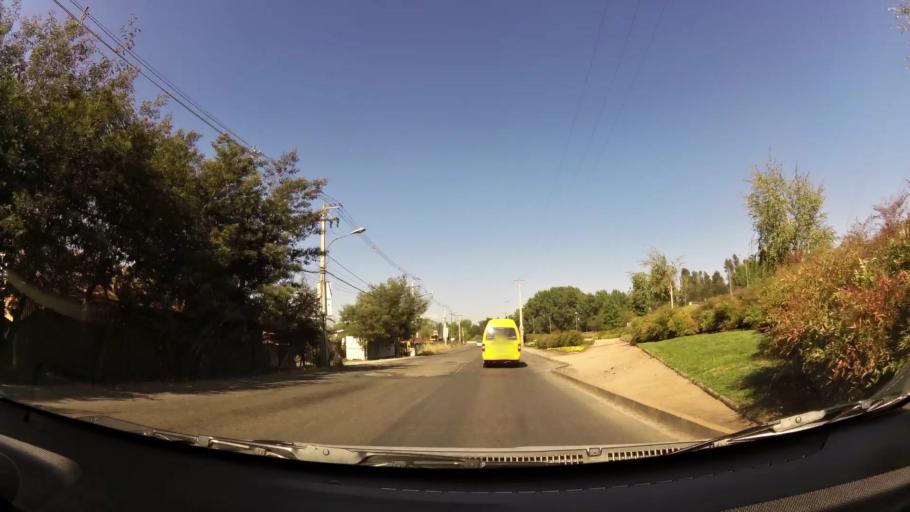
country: CL
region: Maule
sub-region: Provincia de Talca
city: Talca
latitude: -35.3993
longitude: -71.6224
